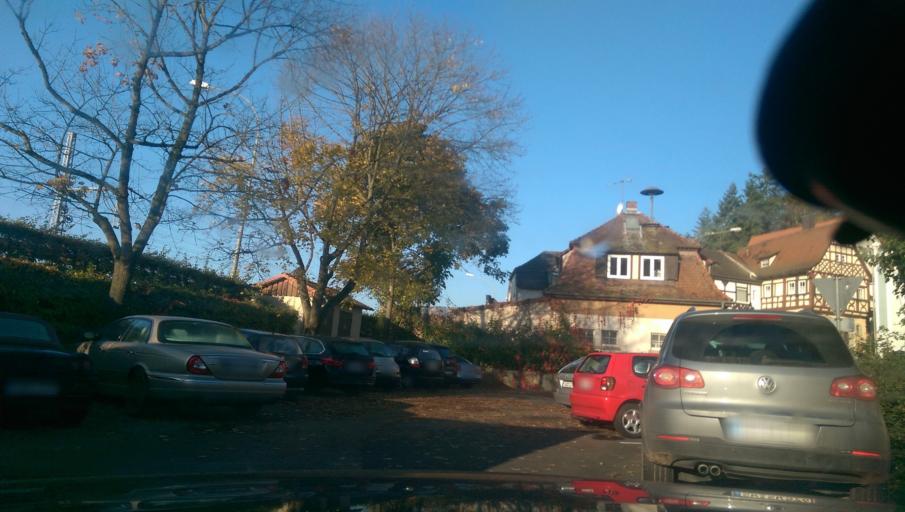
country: DE
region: Bavaria
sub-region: Regierungsbezirk Unterfranken
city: Schonungen
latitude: 50.0567
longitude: 10.2875
